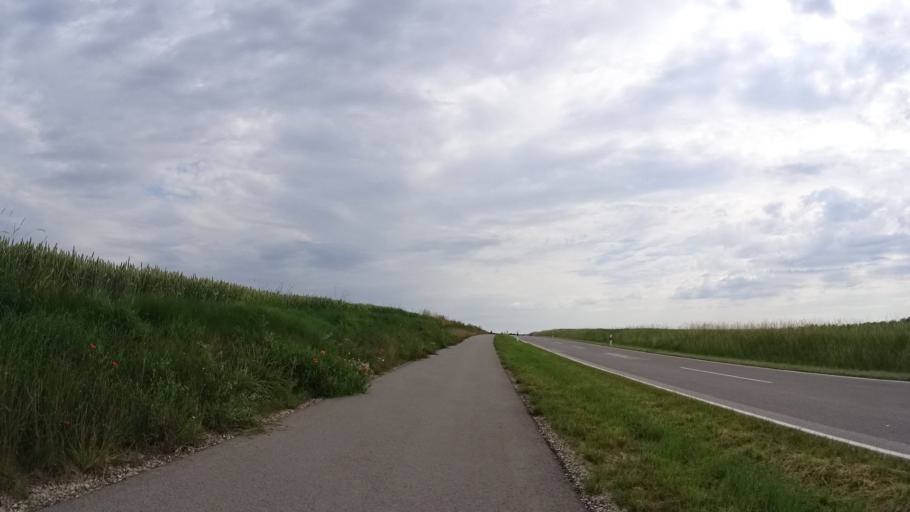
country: DE
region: Bavaria
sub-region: Upper Bavaria
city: Stammham
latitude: 48.8634
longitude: 11.4722
